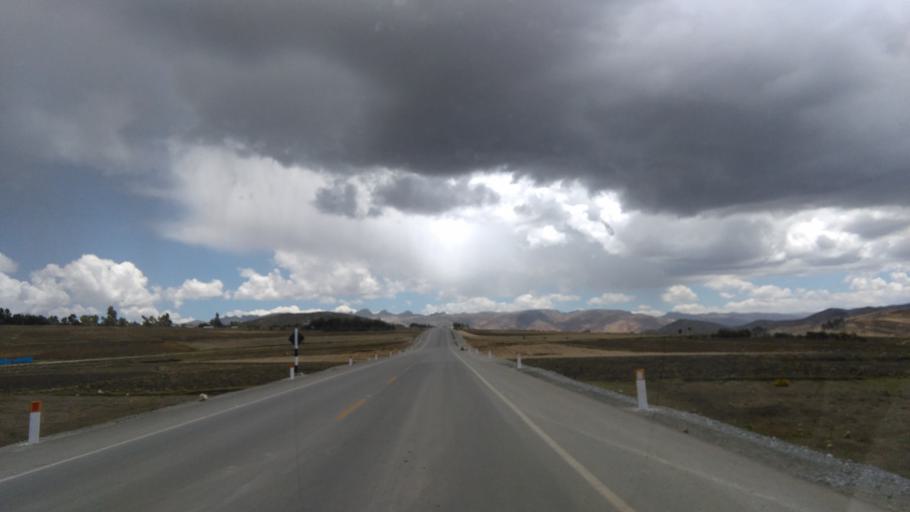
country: PE
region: Apurimac
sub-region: Provincia de Andahuaylas
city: San Jeronimo
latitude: -13.7191
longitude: -73.3498
